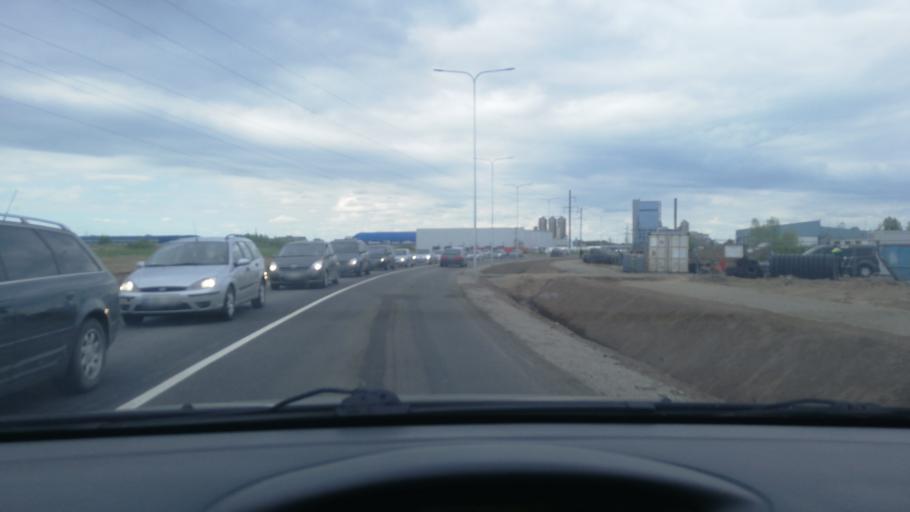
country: LT
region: Klaipedos apskritis
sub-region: Klaipeda
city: Klaipeda
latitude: 55.6838
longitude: 21.1977
